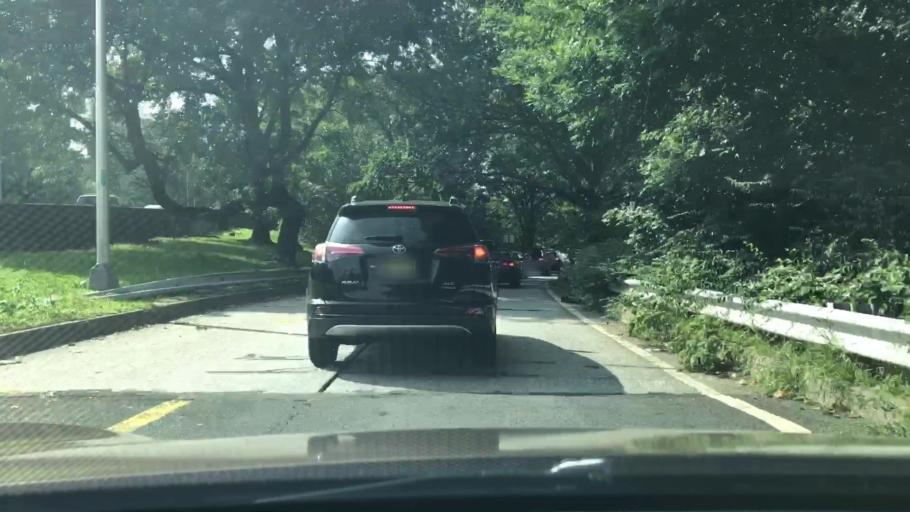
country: US
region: New York
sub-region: New York County
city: Manhattan
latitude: 40.7867
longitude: -73.9836
